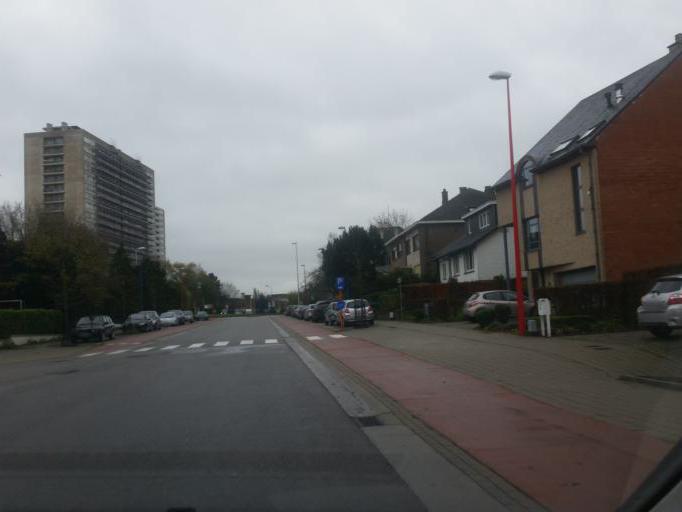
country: BE
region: Flanders
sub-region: Provincie Vlaams-Brabant
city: Grimbergen
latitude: 50.9031
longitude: 4.3572
